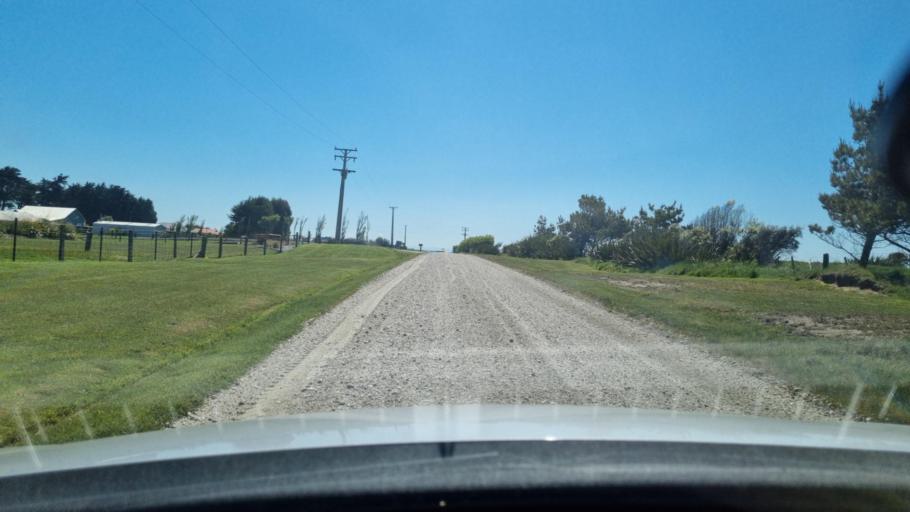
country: NZ
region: Southland
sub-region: Invercargill City
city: Invercargill
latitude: -46.4119
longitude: 168.2634
